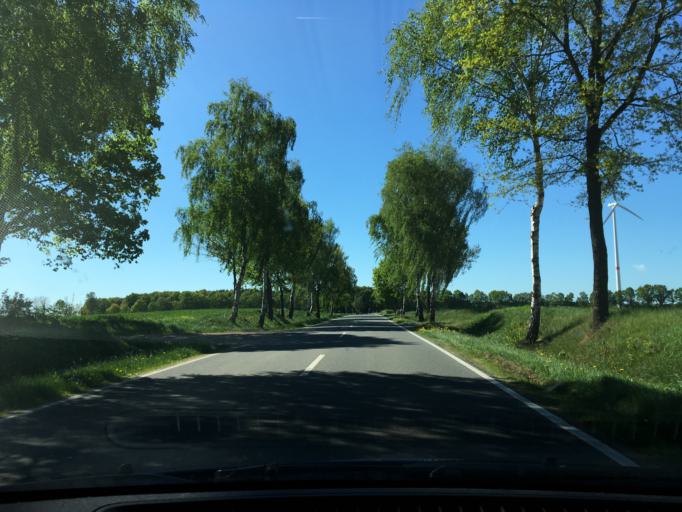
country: DE
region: Lower Saxony
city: Hermannsburg
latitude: 52.8353
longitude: 10.0426
